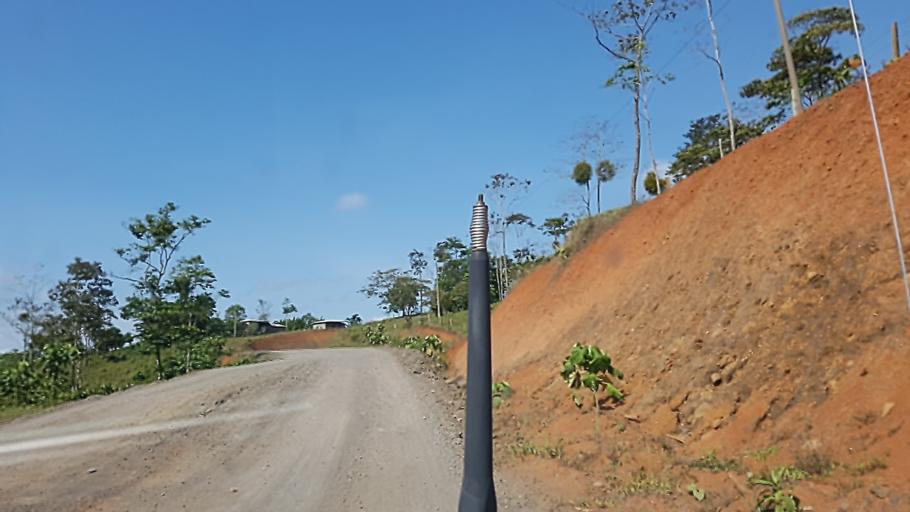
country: NI
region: Atlantico Sur
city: Nueva Guinea
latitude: 11.7856
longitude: -84.1662
